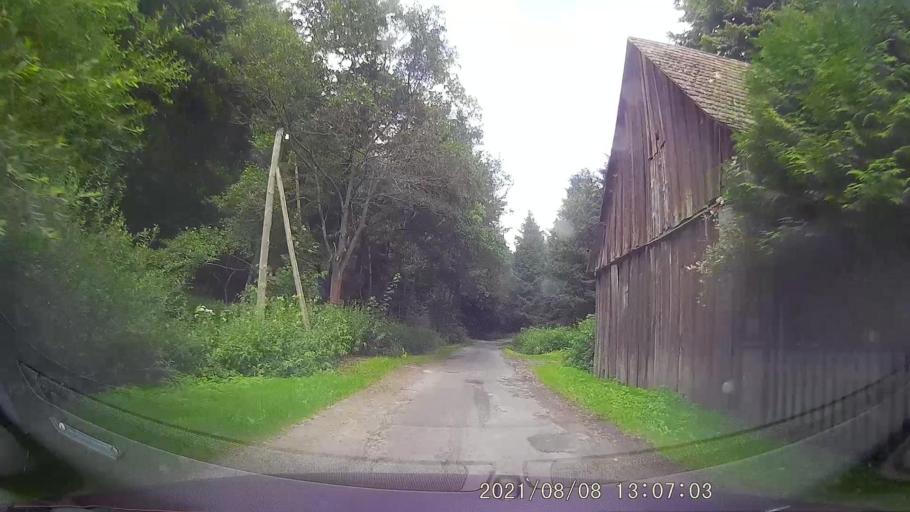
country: PL
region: Lower Silesian Voivodeship
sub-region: Powiat klodzki
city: Lewin Klodzki
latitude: 50.4324
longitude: 16.2984
